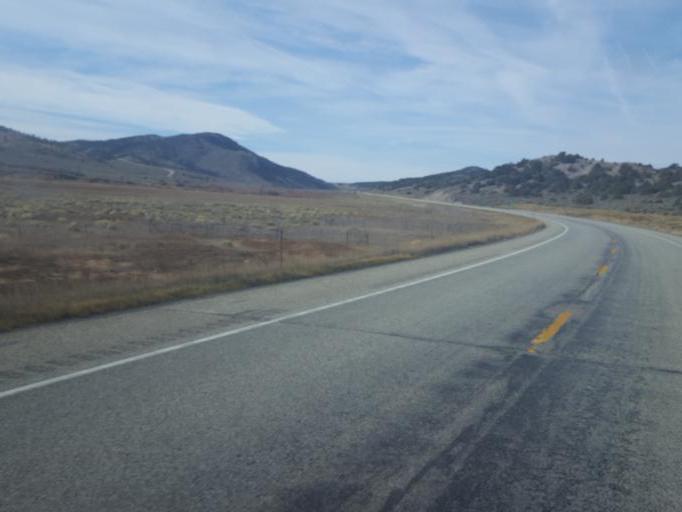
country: US
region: Colorado
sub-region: Costilla County
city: San Luis
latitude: 37.5148
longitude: -105.3095
